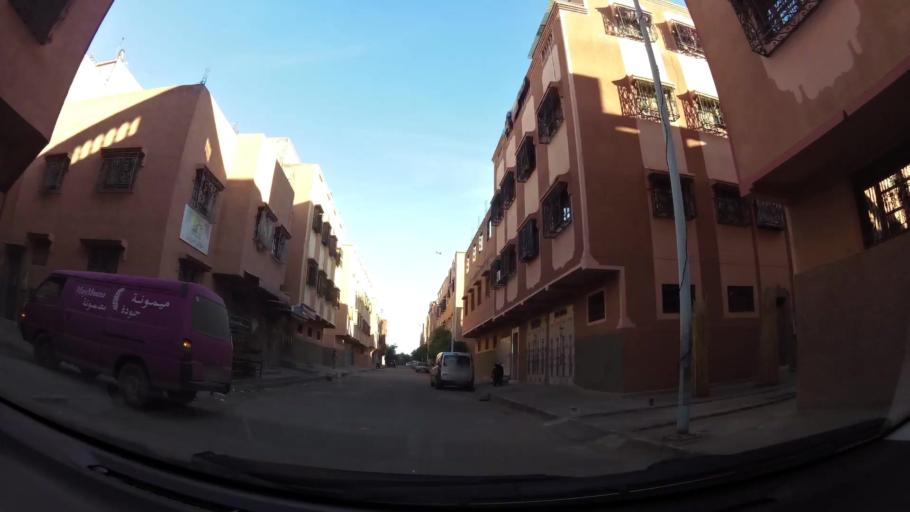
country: MA
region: Marrakech-Tensift-Al Haouz
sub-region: Marrakech
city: Marrakesh
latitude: 31.6154
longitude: -8.0605
